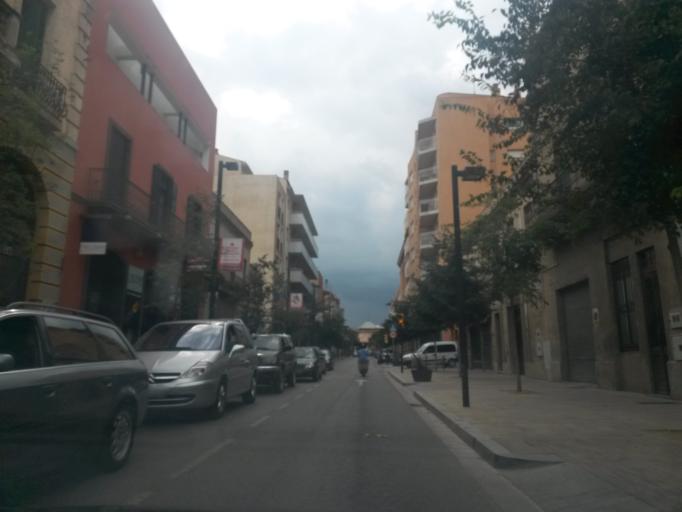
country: ES
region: Catalonia
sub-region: Provincia de Girona
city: Figueres
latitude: 42.2664
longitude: 2.9683
